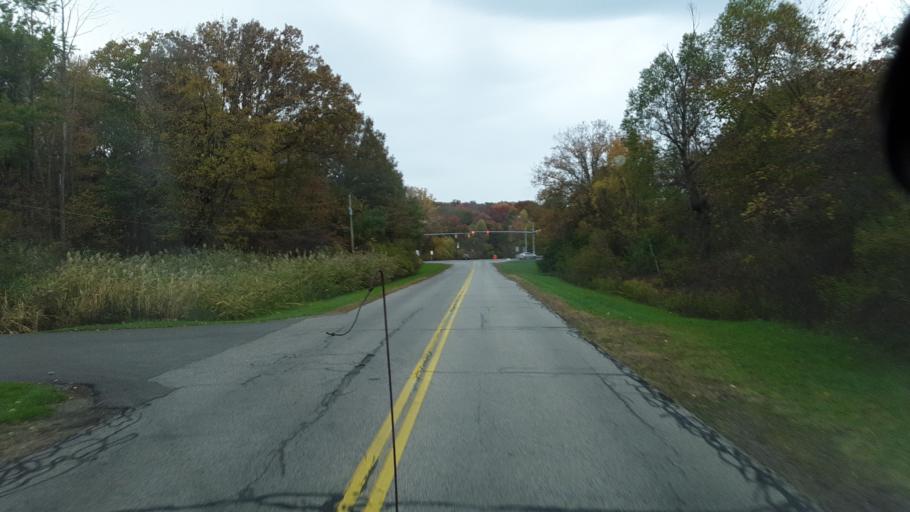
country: US
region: Ohio
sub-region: Portage County
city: Kent
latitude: 41.1329
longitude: -81.3464
